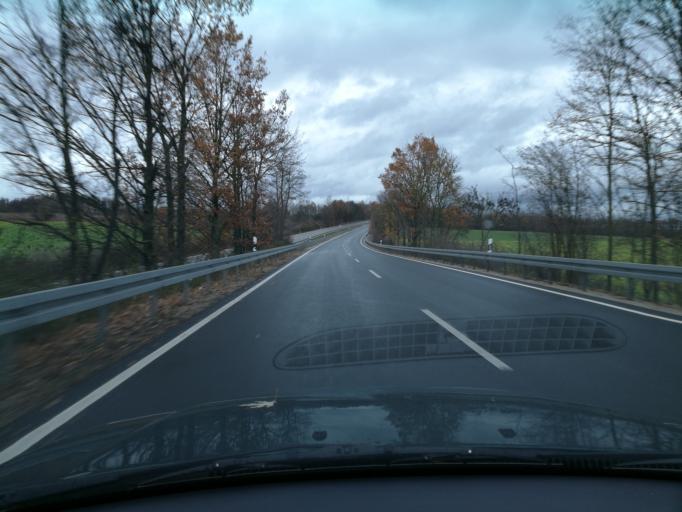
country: DE
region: Bavaria
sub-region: Regierungsbezirk Mittelfranken
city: Zirndorf
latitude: 49.4793
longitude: 10.9312
